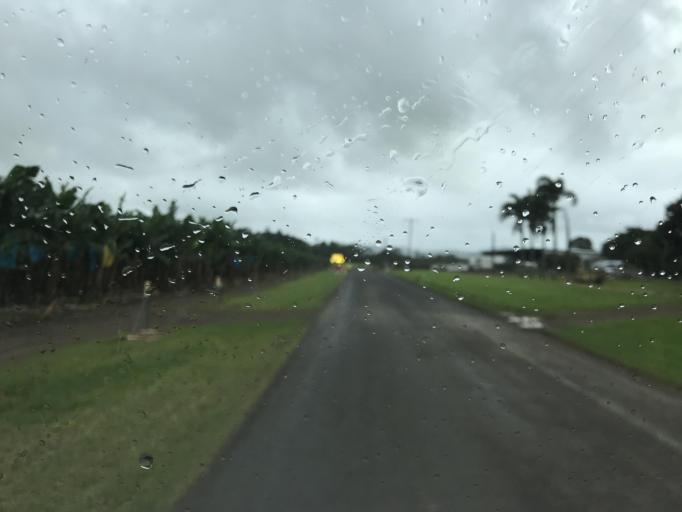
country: AU
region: Queensland
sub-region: Cassowary Coast
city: Innisfail
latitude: -17.5035
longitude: 145.9808
